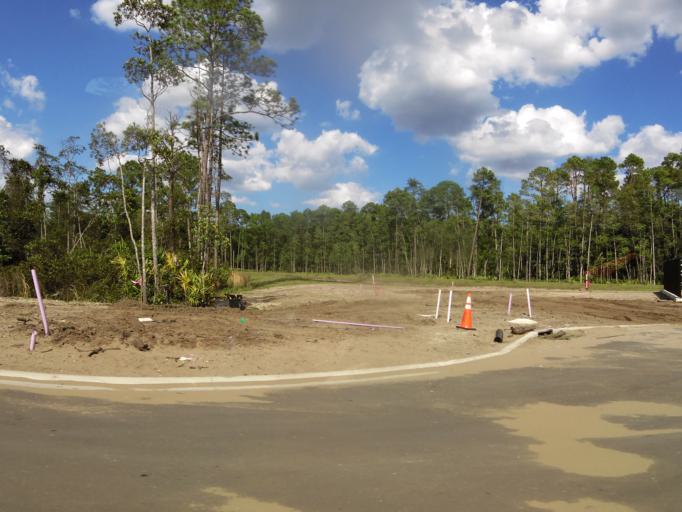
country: US
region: Florida
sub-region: Saint Johns County
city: Palm Valley
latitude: 30.1877
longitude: -81.5002
